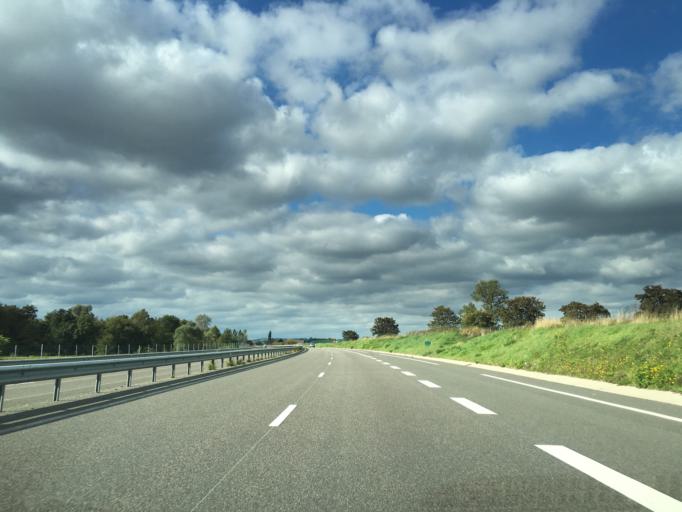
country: FR
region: Lorraine
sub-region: Departement de Meurthe-et-Moselle
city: Chanteheux
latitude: 48.5408
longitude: 6.5735
